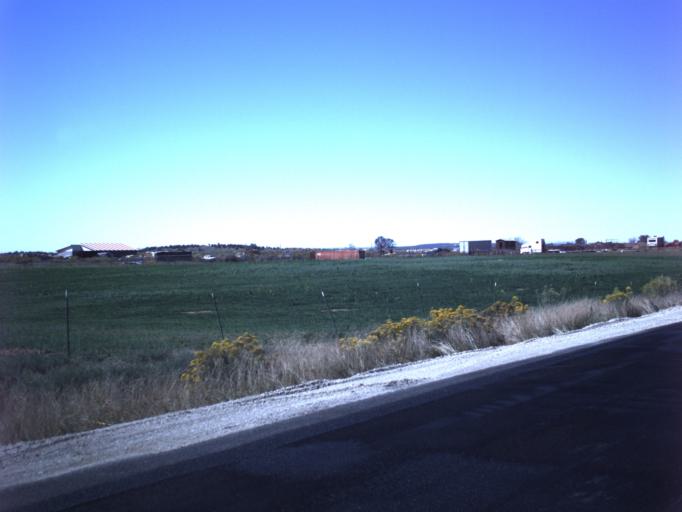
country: US
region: Utah
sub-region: San Juan County
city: Blanding
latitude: 37.5736
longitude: -109.4897
